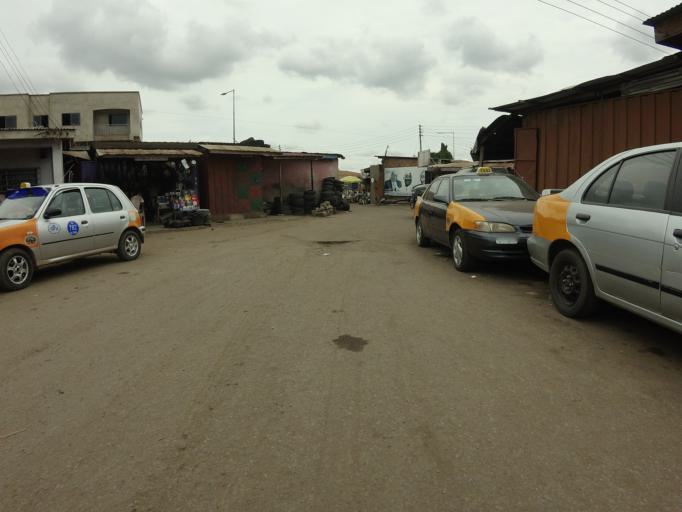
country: GH
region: Greater Accra
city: Accra
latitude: 5.5905
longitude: -0.2172
